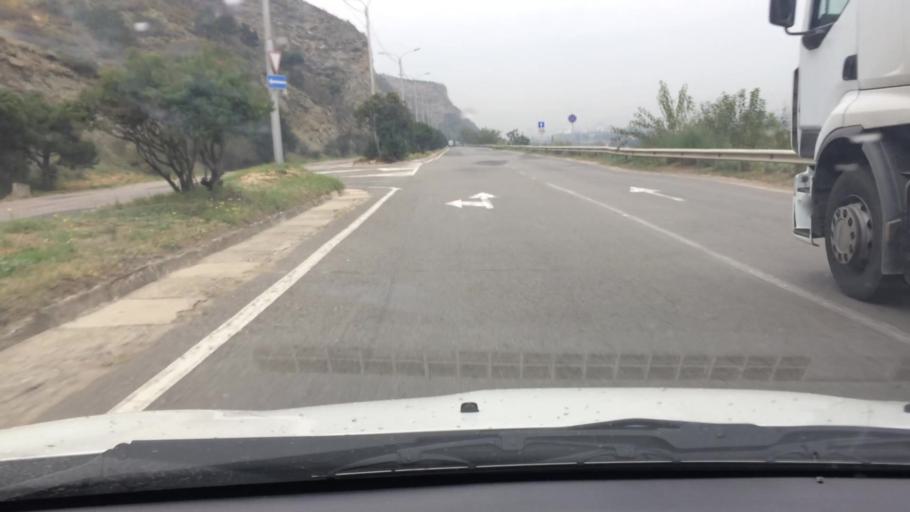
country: GE
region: T'bilisi
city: Tbilisi
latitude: 41.6525
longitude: 44.9030
